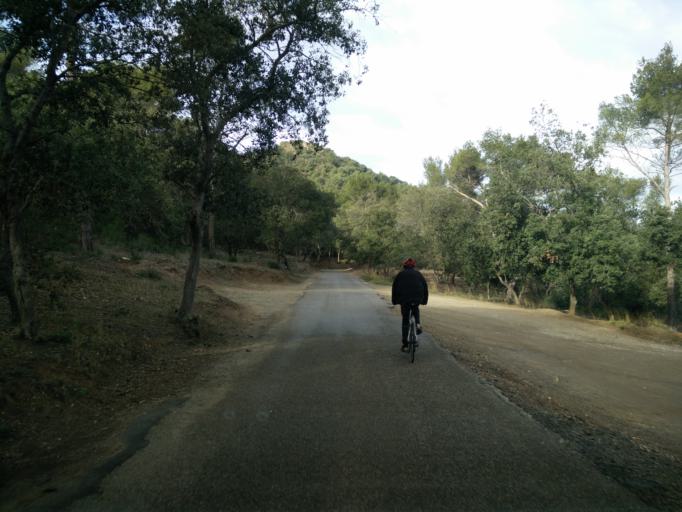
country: FR
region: Provence-Alpes-Cote d'Azur
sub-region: Departement du Var
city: Six-Fours-les-Plages
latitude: 43.0606
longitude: 5.8326
